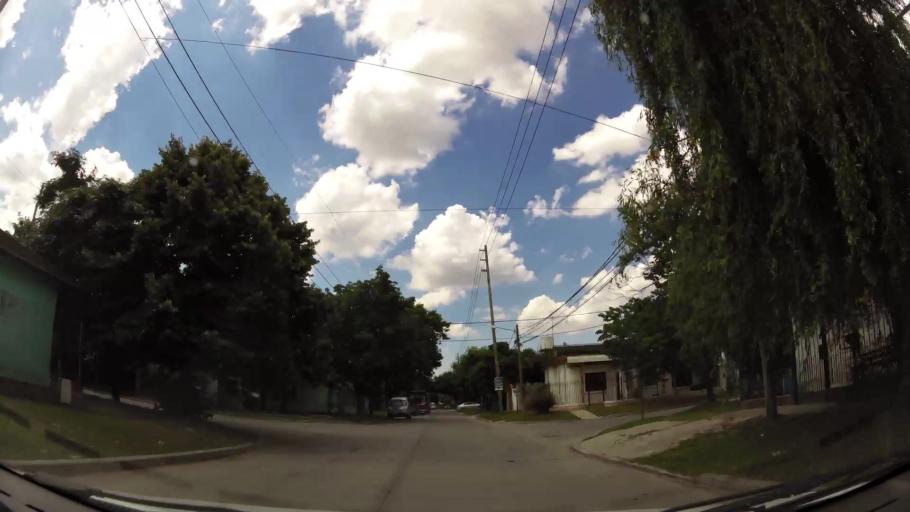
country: AR
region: Buenos Aires
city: Ituzaingo
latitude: -34.6465
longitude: -58.6851
